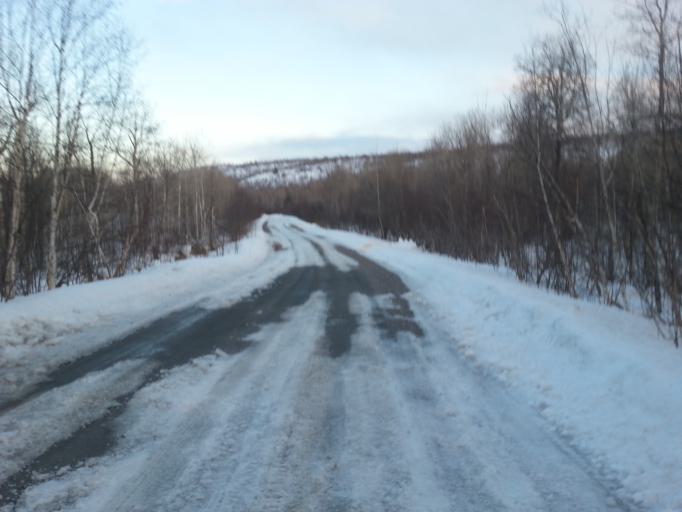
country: CA
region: Ontario
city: Greater Sudbury
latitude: 46.5911
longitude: -80.9981
